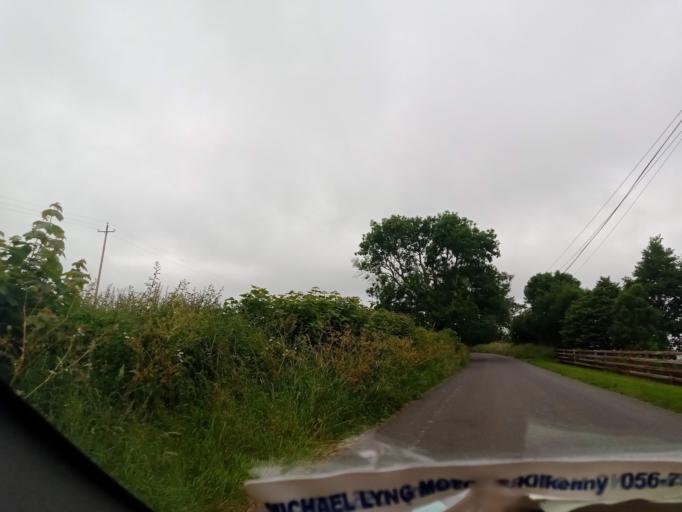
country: IE
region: Leinster
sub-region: Kilkenny
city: Ballyragget
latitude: 52.7502
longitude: -7.4315
